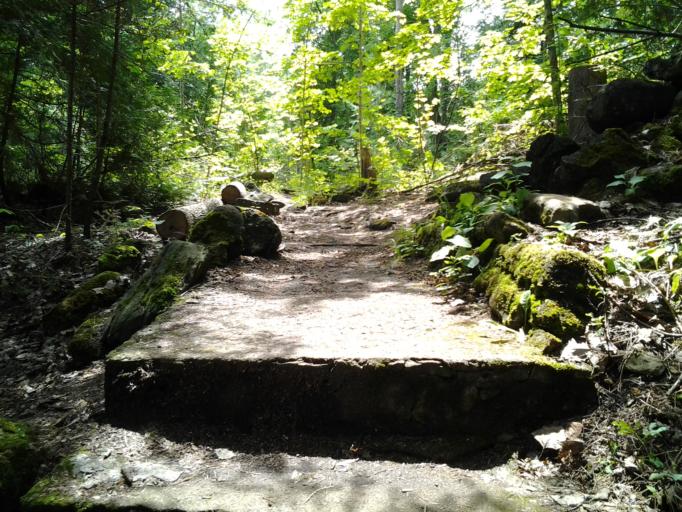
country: CA
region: Ontario
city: Orangeville
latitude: 43.7945
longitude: -80.0107
